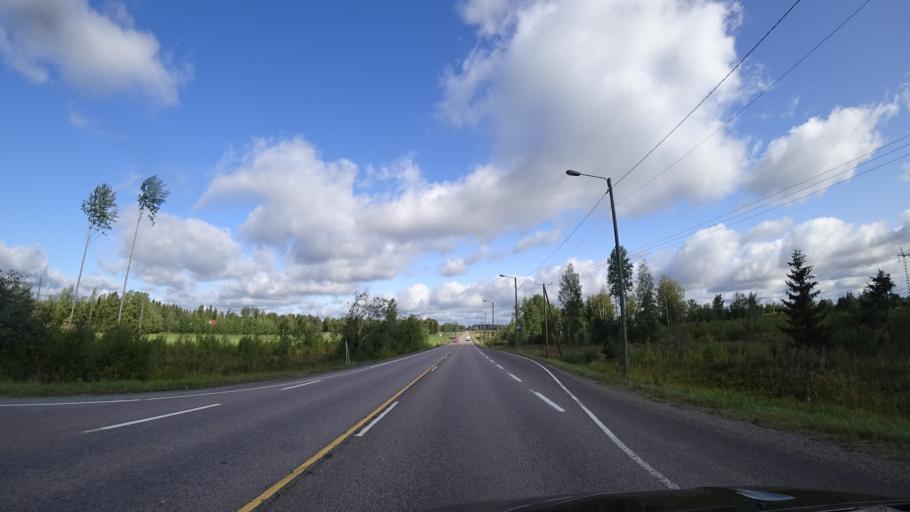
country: FI
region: Uusimaa
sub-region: Helsinki
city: Nurmijaervi
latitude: 60.5109
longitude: 24.9279
